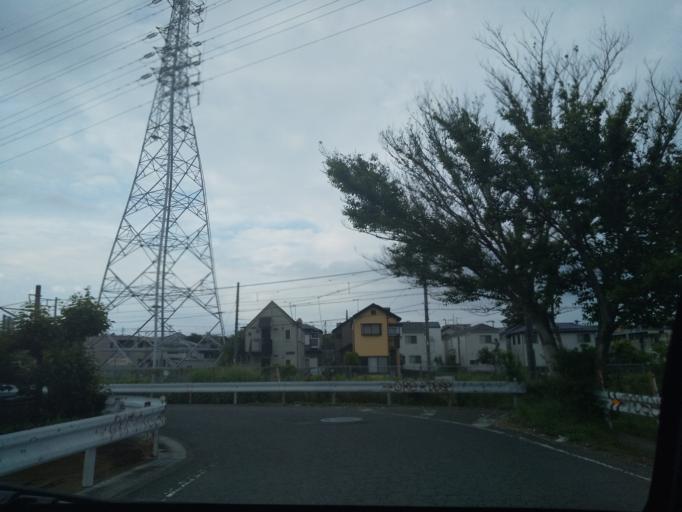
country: JP
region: Kanagawa
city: Zama
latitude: 35.4968
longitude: 139.3847
